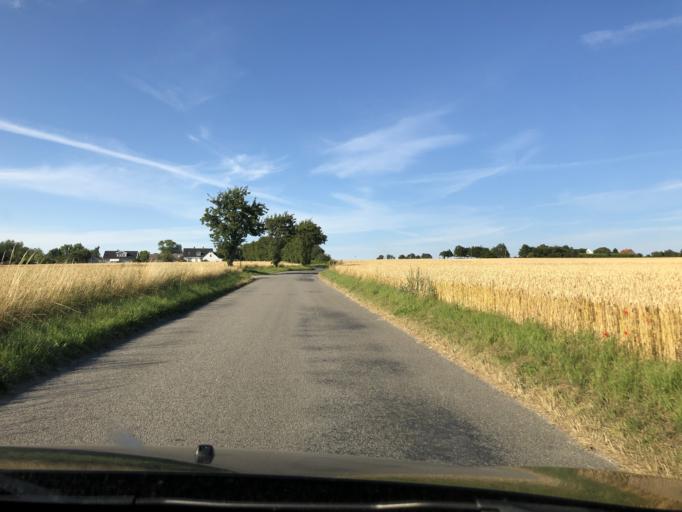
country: DK
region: South Denmark
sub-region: AEro Kommune
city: AEroskobing
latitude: 54.8633
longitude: 10.3677
